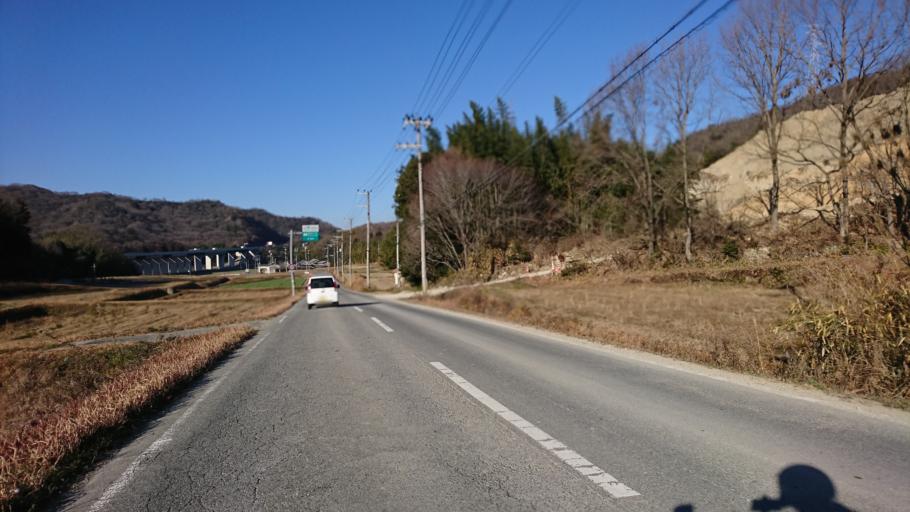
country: JP
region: Hyogo
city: Ono
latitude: 34.8394
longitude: 134.8709
